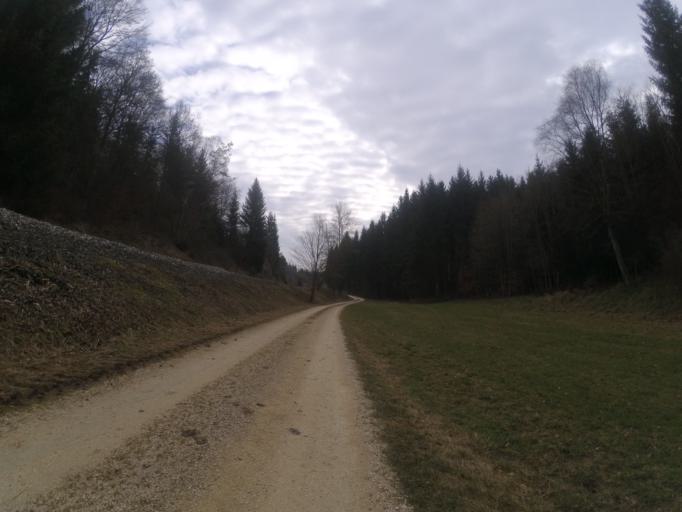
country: DE
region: Baden-Wuerttemberg
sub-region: Tuebingen Region
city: Mehrstetten
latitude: 48.3615
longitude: 9.5417
